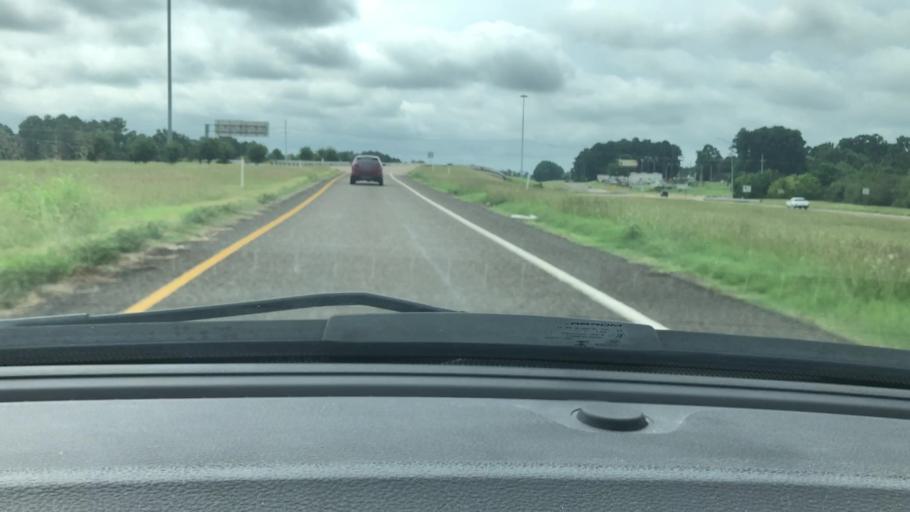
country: US
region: Texas
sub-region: Bowie County
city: Wake Village
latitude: 33.4341
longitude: -94.0971
